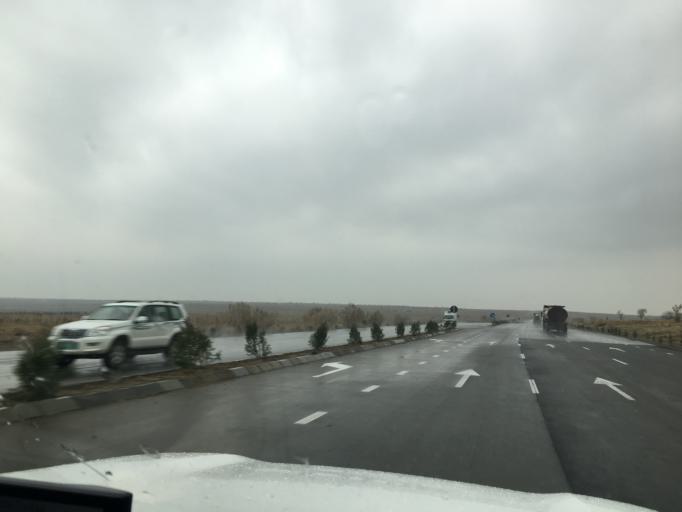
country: TM
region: Ahal
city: Annau
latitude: 37.8731
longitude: 58.6505
